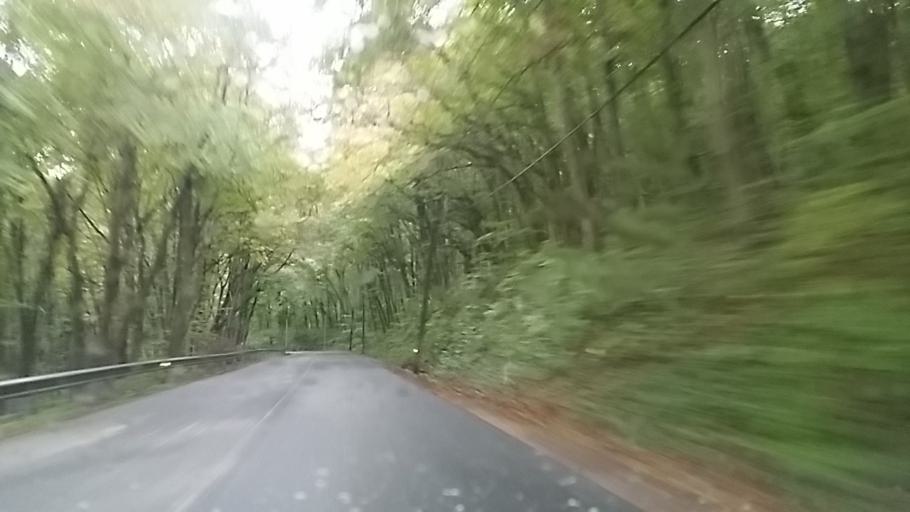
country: HU
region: Komarom-Esztergom
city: Kesztolc
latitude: 47.7372
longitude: 18.8128
